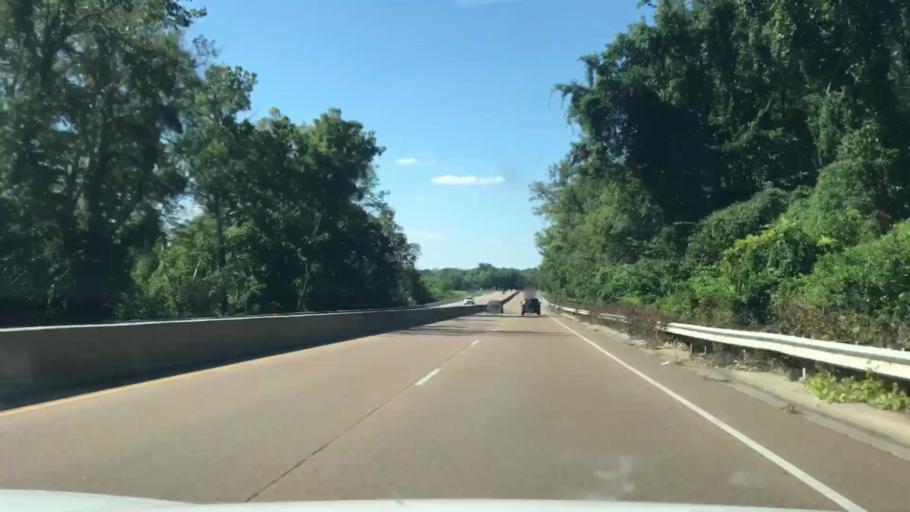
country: US
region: Illinois
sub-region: Saint Clair County
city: Alorton
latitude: 38.5521
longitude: -90.0729
